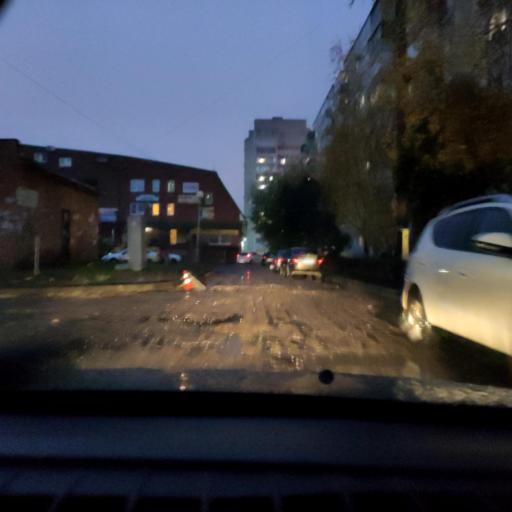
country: RU
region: Samara
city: Tol'yatti
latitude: 53.5456
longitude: 49.3594
